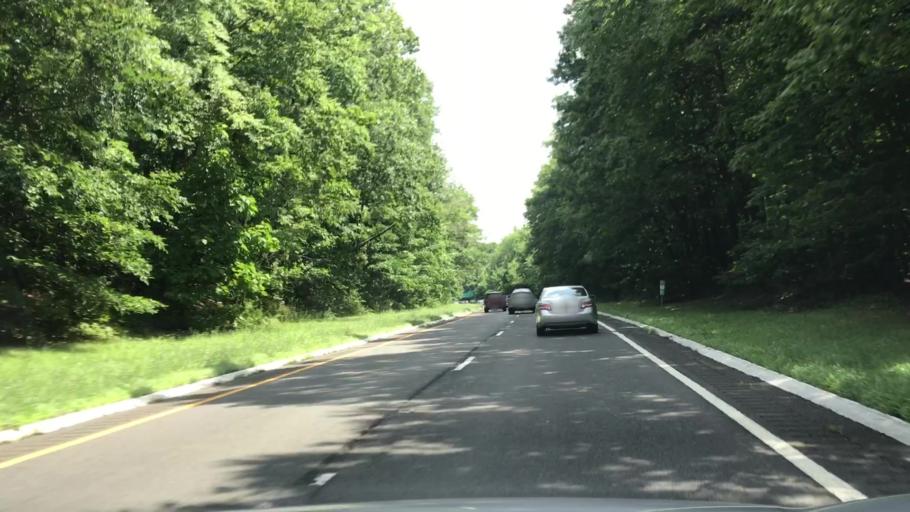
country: US
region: New York
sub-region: Rockland County
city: New Square
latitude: 41.1274
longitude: -74.0147
